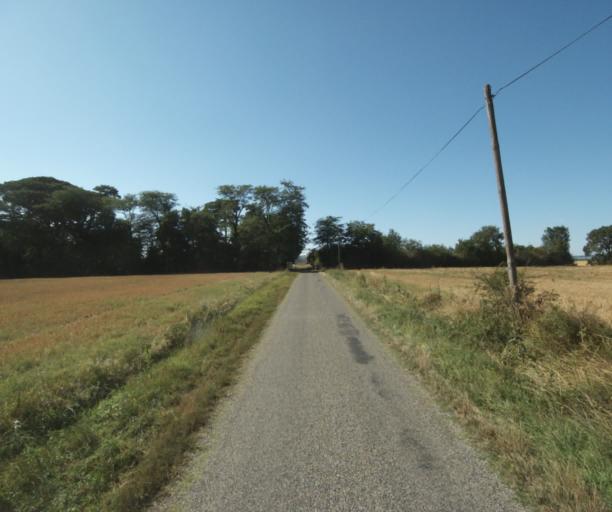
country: FR
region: Midi-Pyrenees
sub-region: Departement de la Haute-Garonne
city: Revel
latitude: 43.4682
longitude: 1.9727
